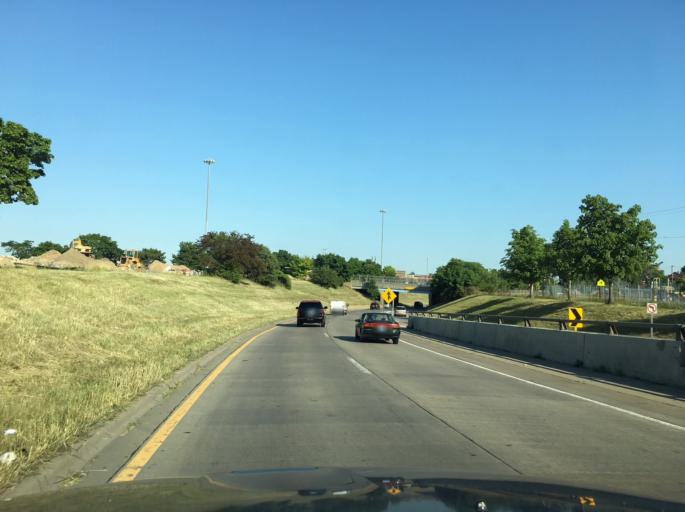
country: US
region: Michigan
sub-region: Wayne County
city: Hamtramck
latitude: 42.3661
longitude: -83.0588
